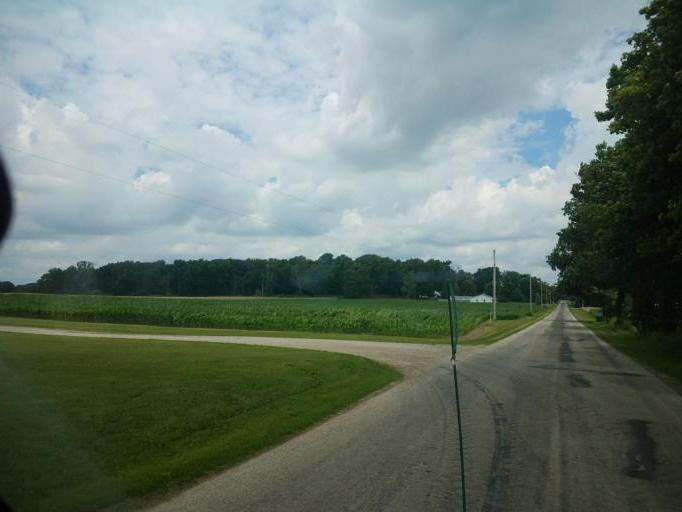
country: US
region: Ohio
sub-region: Richland County
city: Shelby
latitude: 40.9330
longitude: -82.7050
